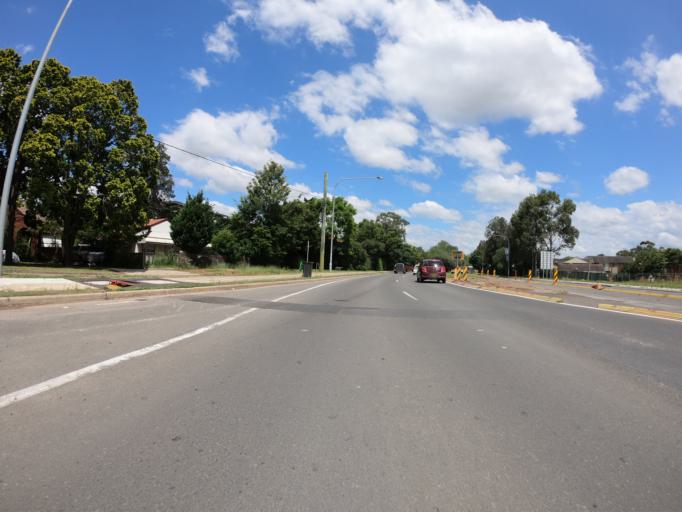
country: AU
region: New South Wales
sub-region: Penrith Municipality
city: Penrith
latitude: -33.7533
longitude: 150.6874
